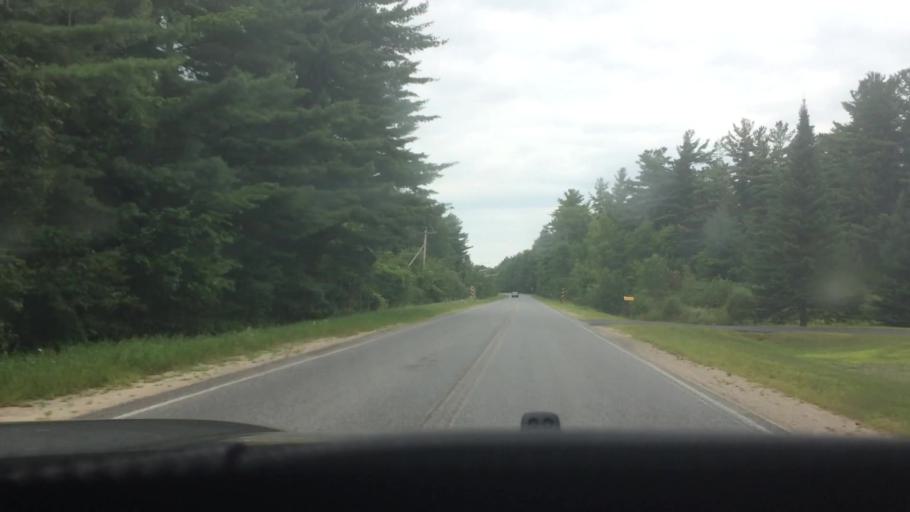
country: US
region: New York
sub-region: St. Lawrence County
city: Hannawa Falls
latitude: 44.5472
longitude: -74.9307
